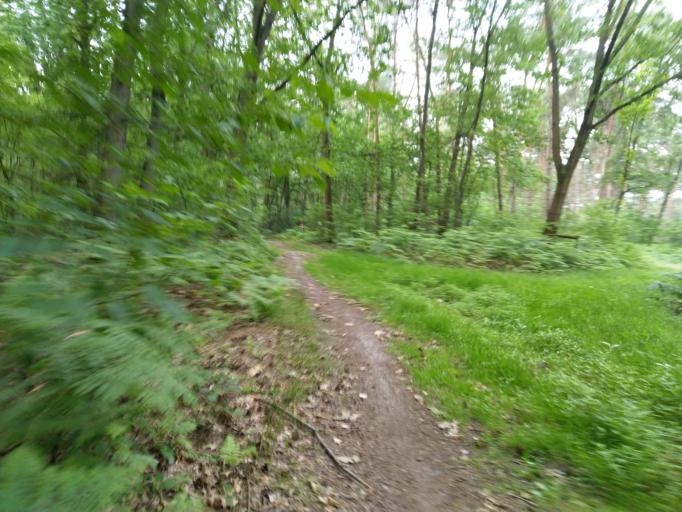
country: BE
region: Wallonia
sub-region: Province du Hainaut
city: Jurbise
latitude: 50.4997
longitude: 3.8755
